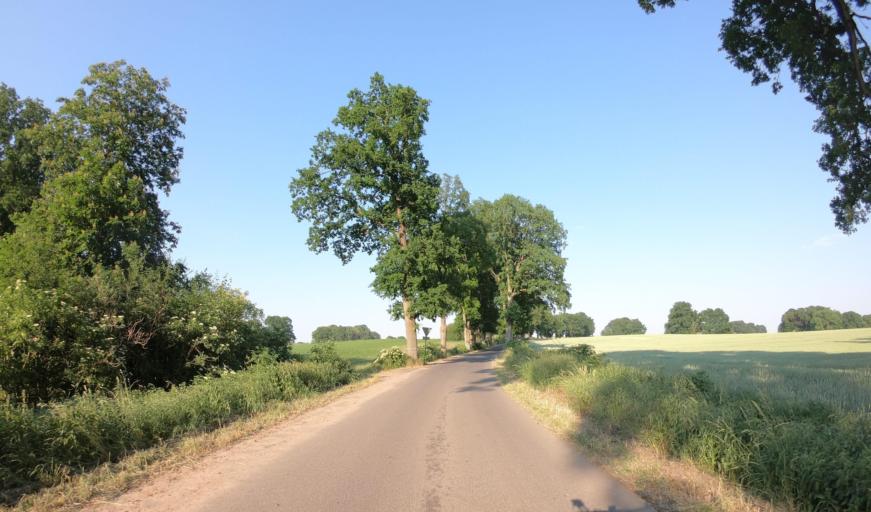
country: PL
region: West Pomeranian Voivodeship
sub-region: Powiat lobeski
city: Radowo Male
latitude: 53.6374
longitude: 15.3783
